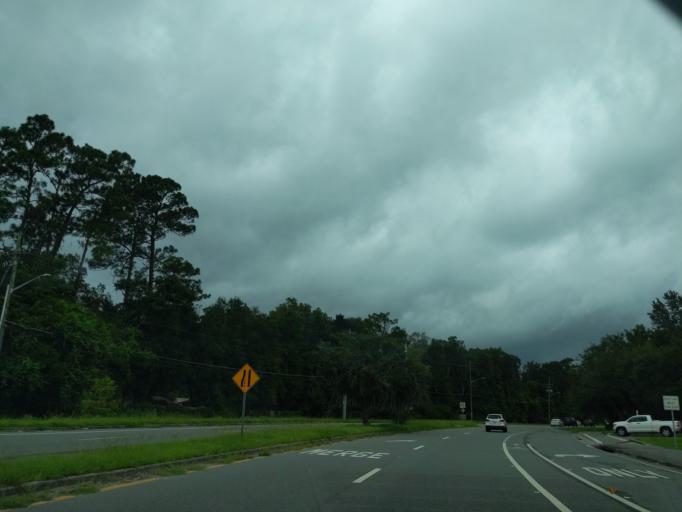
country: US
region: Florida
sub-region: Alachua County
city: Gainesville
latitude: 29.6017
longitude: -82.4223
